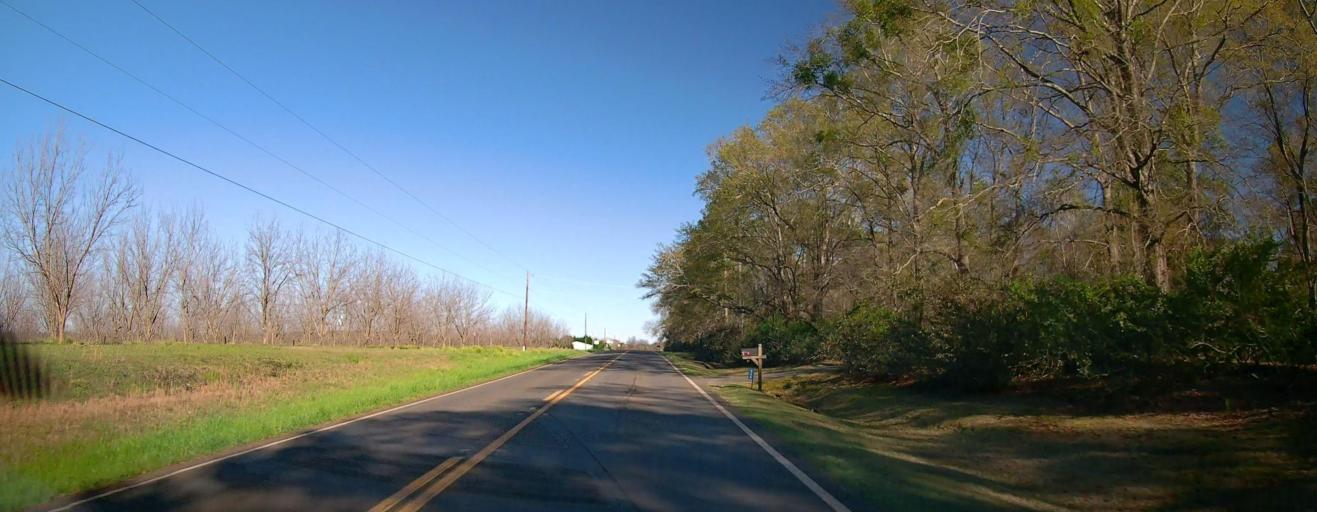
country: US
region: Georgia
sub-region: Macon County
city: Marshallville
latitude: 32.4561
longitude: -83.9268
